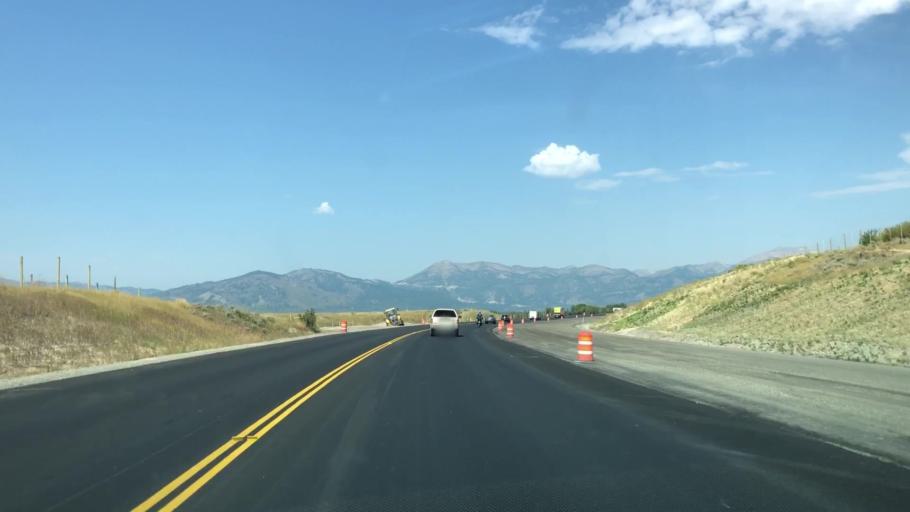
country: US
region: Wyoming
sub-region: Teton County
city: South Park
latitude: 43.4096
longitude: -110.7683
